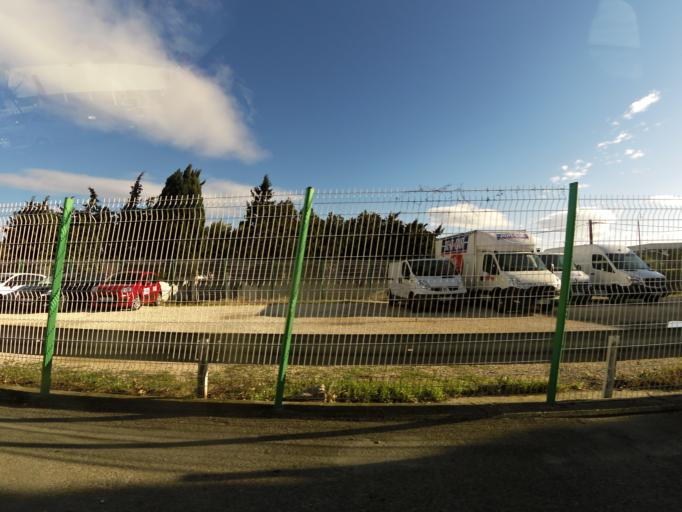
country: FR
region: Languedoc-Roussillon
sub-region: Departement du Gard
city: Nimes
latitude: 43.8129
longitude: 4.3327
